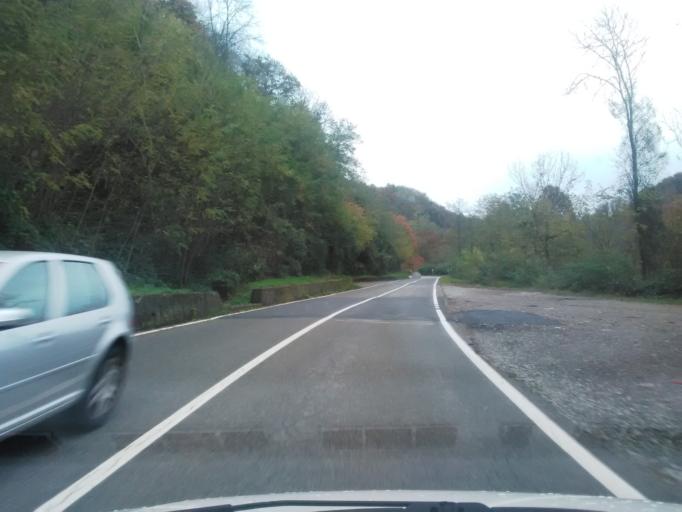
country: IT
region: Piedmont
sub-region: Provincia di Vercelli
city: Valduggia
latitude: 45.7379
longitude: 8.3508
